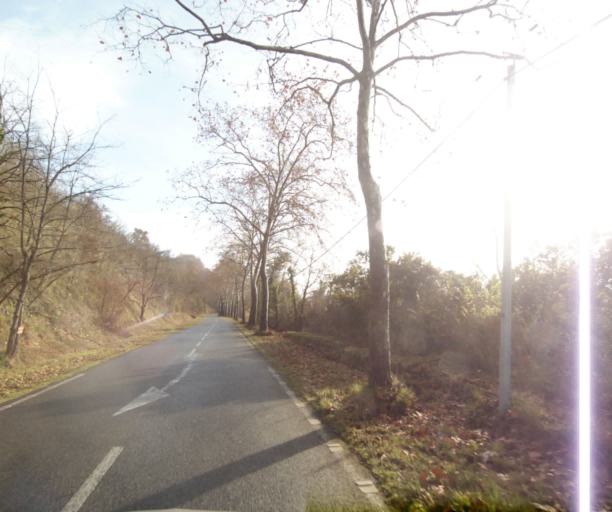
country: FR
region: Midi-Pyrenees
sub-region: Departement de la Haute-Garonne
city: Villemur-sur-Tarn
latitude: 43.8560
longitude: 1.5131
